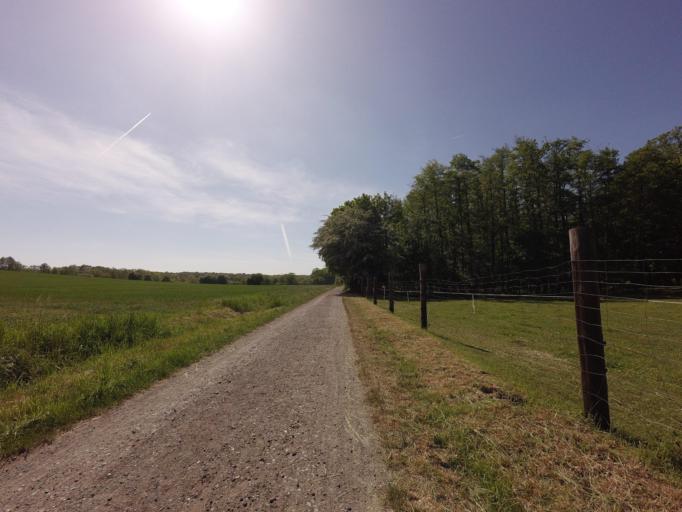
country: DE
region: Lower Saxony
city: Cremlingen
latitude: 52.2935
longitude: 10.6425
